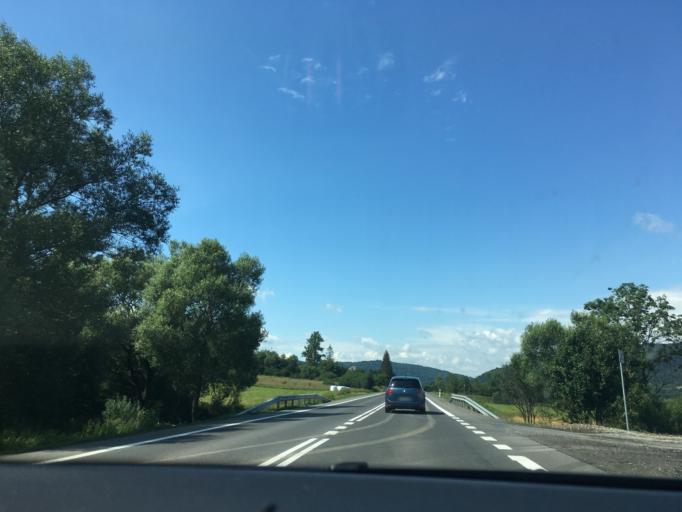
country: PL
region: Subcarpathian Voivodeship
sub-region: Powiat krosnienski
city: Dukla
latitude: 49.4952
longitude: 21.7021
